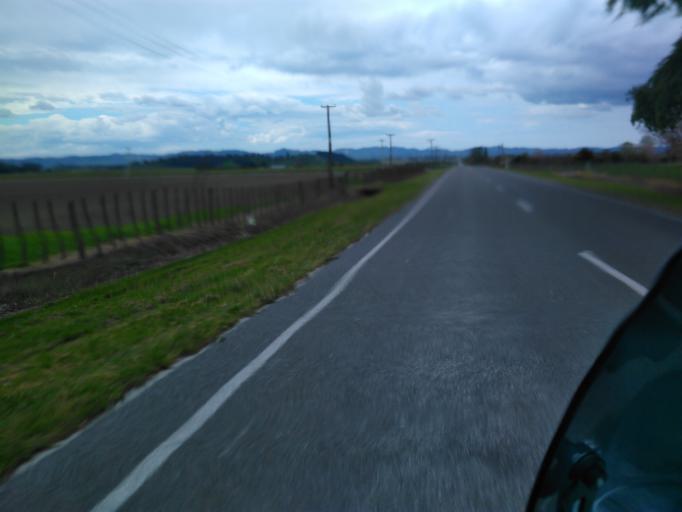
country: NZ
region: Gisborne
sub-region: Gisborne District
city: Gisborne
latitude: -38.6455
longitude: 177.8574
